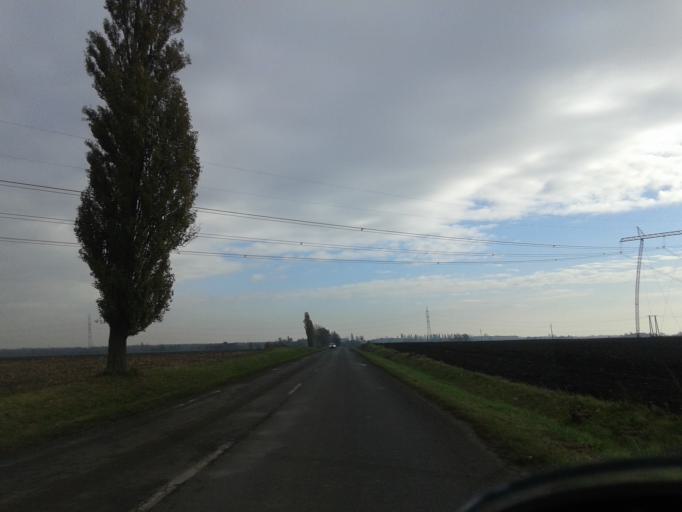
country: HU
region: Fejer
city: Pusztaszabolcs
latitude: 47.1345
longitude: 18.7926
